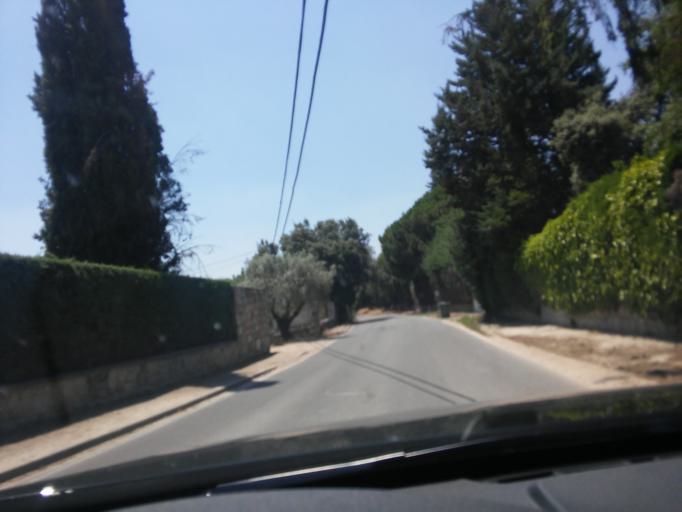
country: ES
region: Madrid
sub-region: Provincia de Madrid
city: Navalquejigo
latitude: 40.6143
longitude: -4.0407
